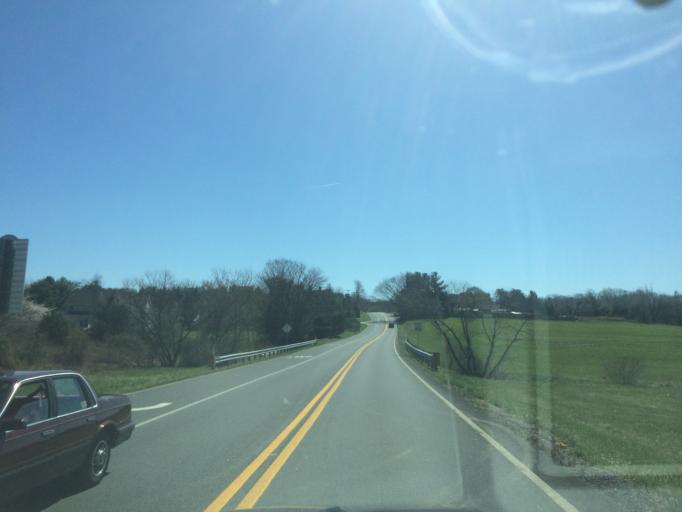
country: US
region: Maryland
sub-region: Carroll County
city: Westminster
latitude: 39.5411
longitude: -77.0062
